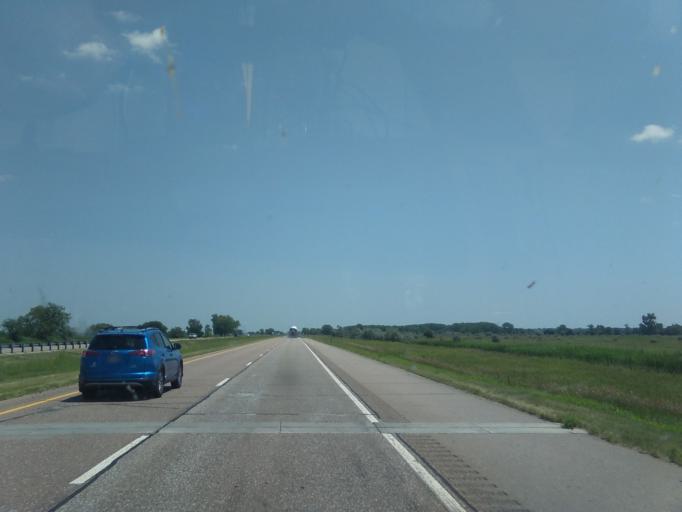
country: US
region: Nebraska
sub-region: Dawson County
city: Cozad
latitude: 40.8724
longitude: -100.0522
